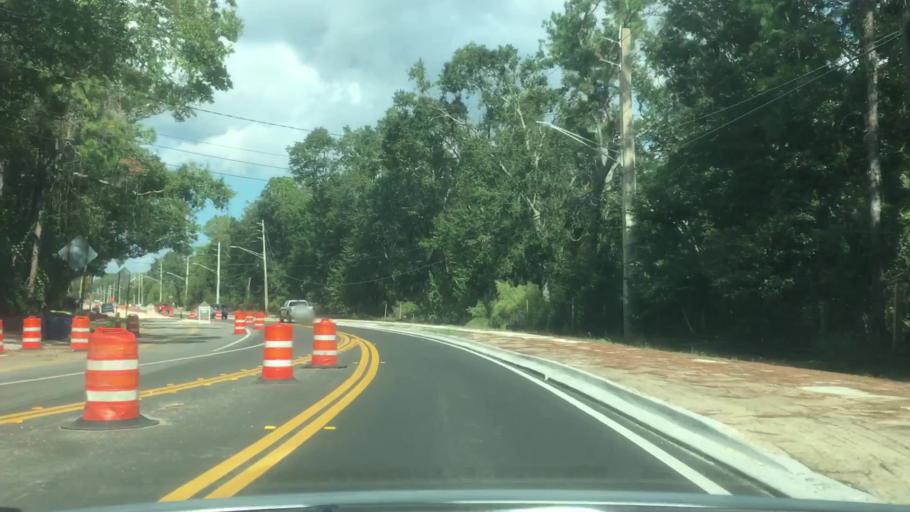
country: US
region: Florida
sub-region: Duval County
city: Atlantic Beach
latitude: 30.3399
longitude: -81.4619
